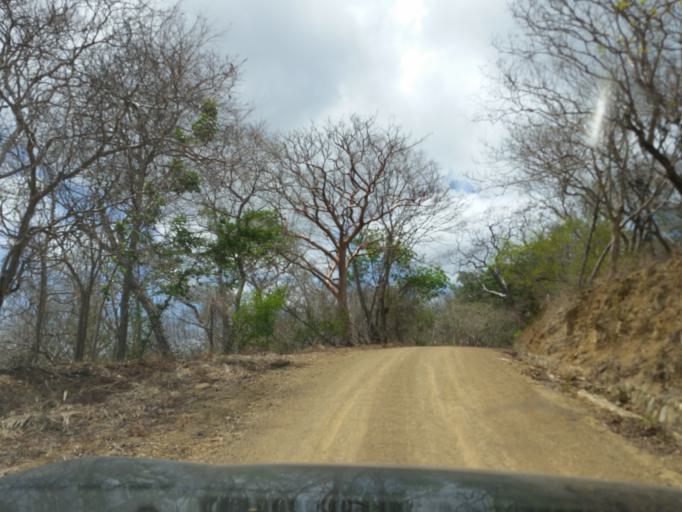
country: NI
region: Rivas
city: Tola
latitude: 11.4297
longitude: -86.0752
